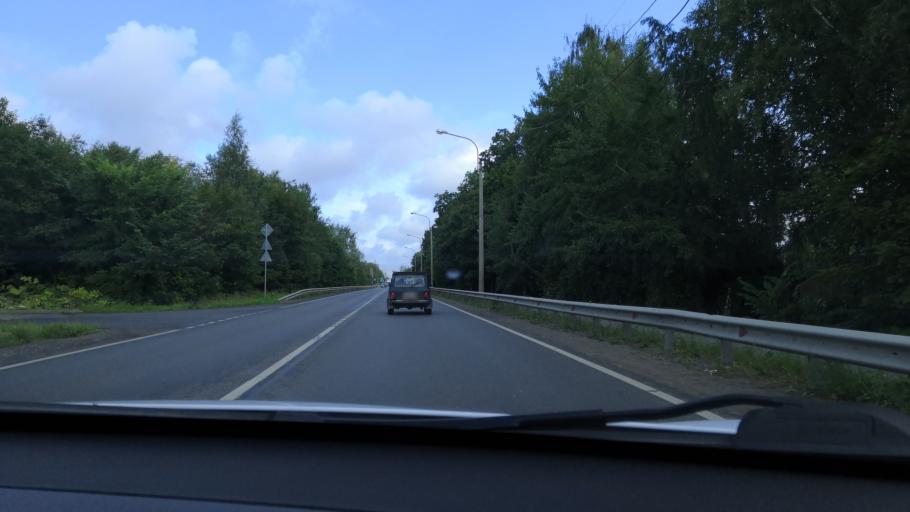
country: RU
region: St.-Petersburg
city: Tyarlevo
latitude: 59.6988
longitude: 30.4416
